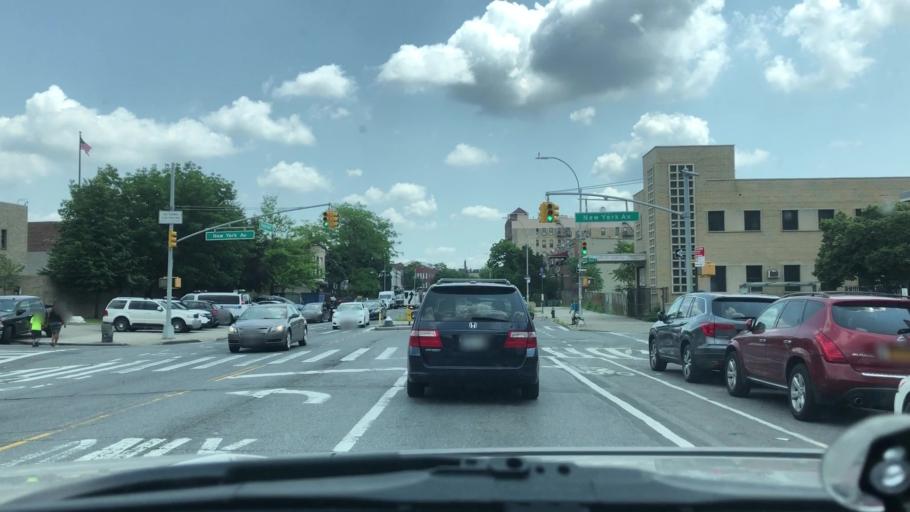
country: US
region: New York
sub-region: Kings County
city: Brooklyn
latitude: 40.6640
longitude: -73.9485
